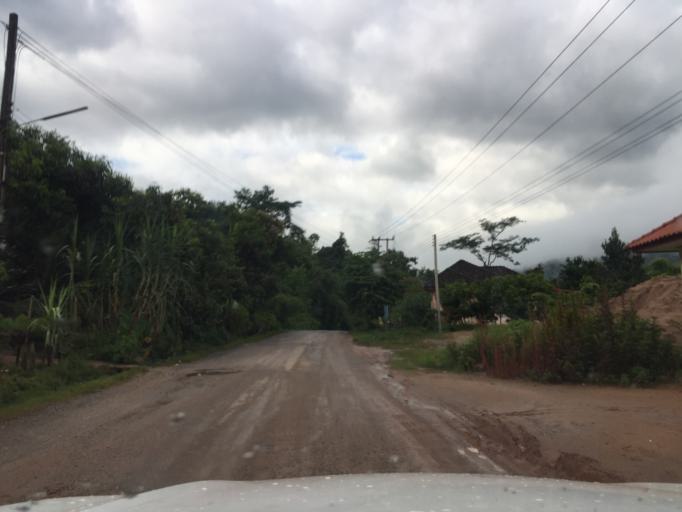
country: LA
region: Oudomxai
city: Muang La
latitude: 20.8519
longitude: 102.1087
